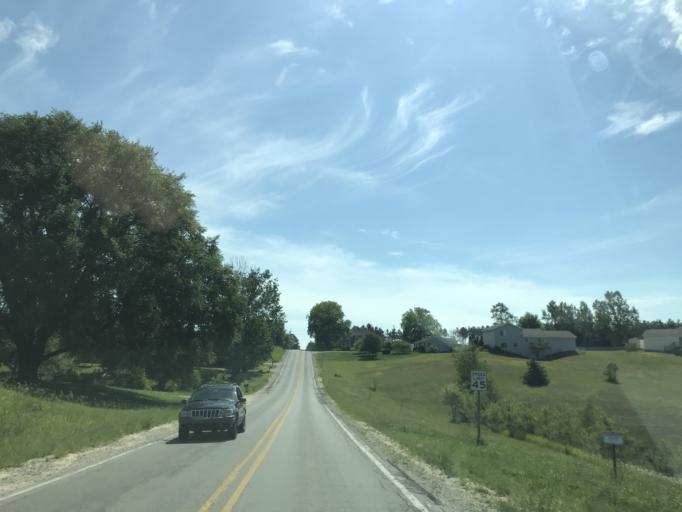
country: US
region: Michigan
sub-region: Grand Traverse County
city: Traverse City
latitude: 44.6575
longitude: -85.6639
